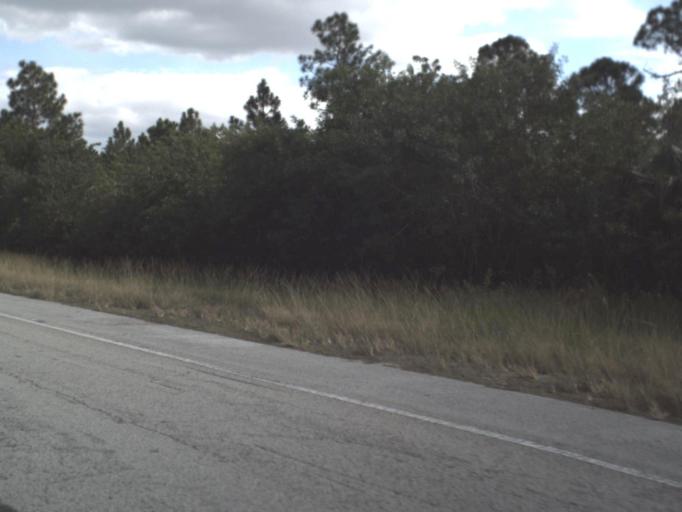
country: US
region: Florida
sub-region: Brevard County
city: Sharpes
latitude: 28.4117
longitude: -80.8135
